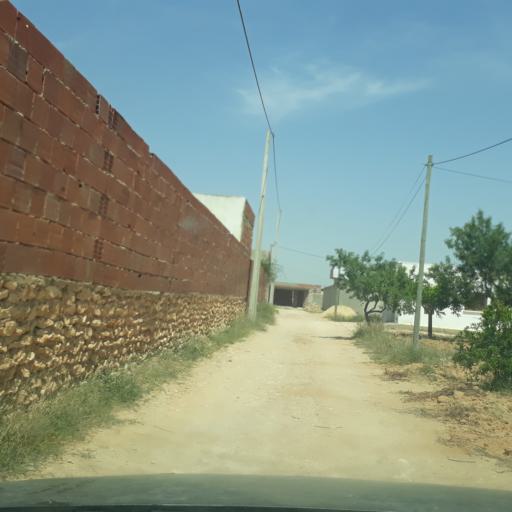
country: TN
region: Safaqis
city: Al Qarmadah
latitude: 34.8243
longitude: 10.7814
